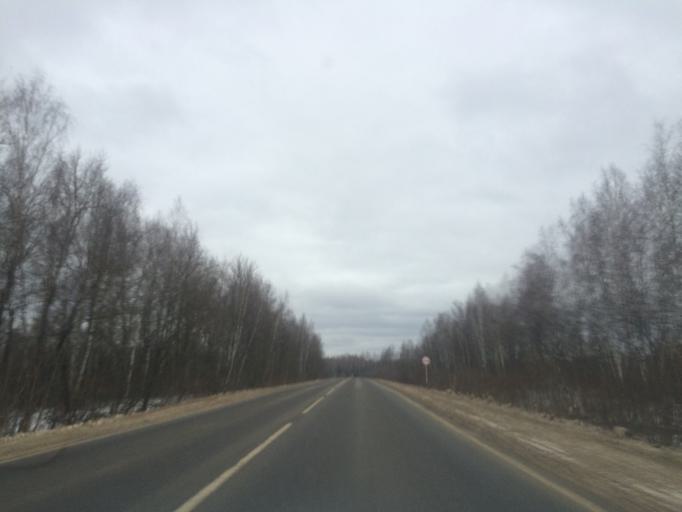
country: RU
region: Tula
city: Odoyev
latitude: 54.0030
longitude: 36.7640
